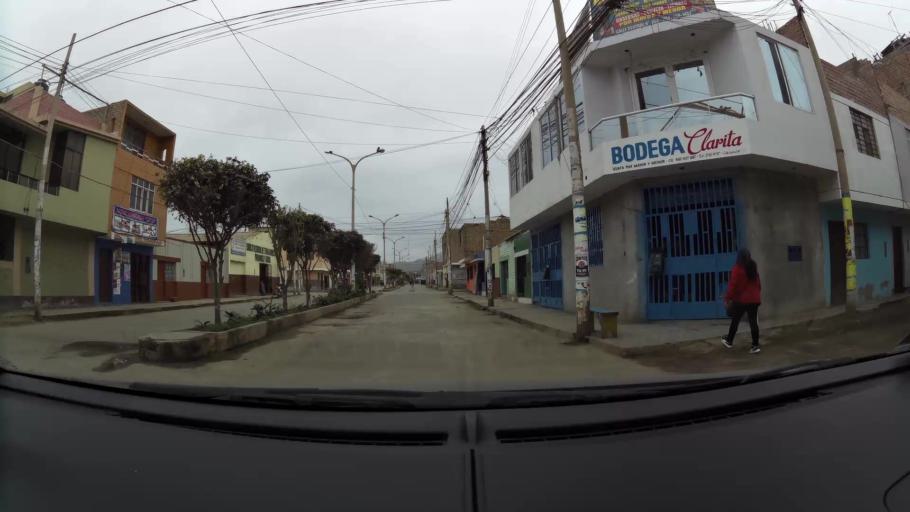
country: PE
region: Lima
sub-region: Barranca
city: Paramonga
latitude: -10.6737
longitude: -77.8169
